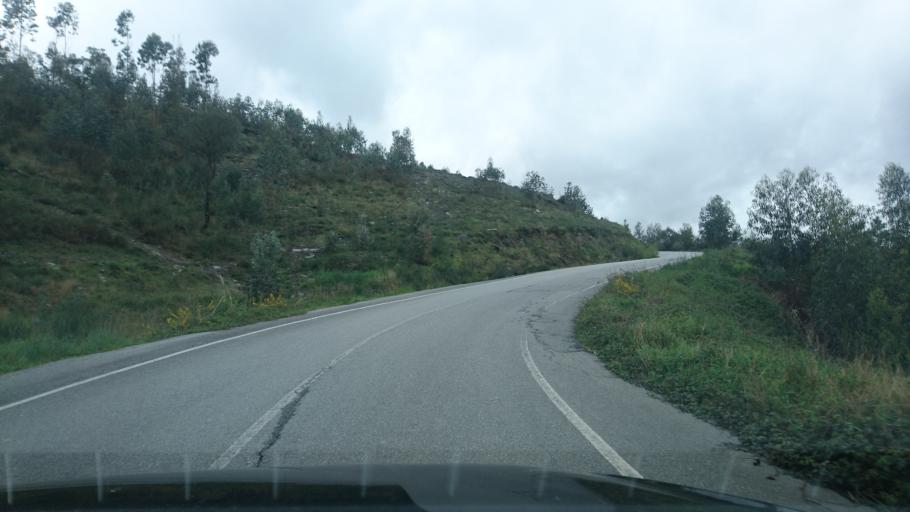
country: PT
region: Porto
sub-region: Paredes
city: Recarei
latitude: 41.1382
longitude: -8.3989
